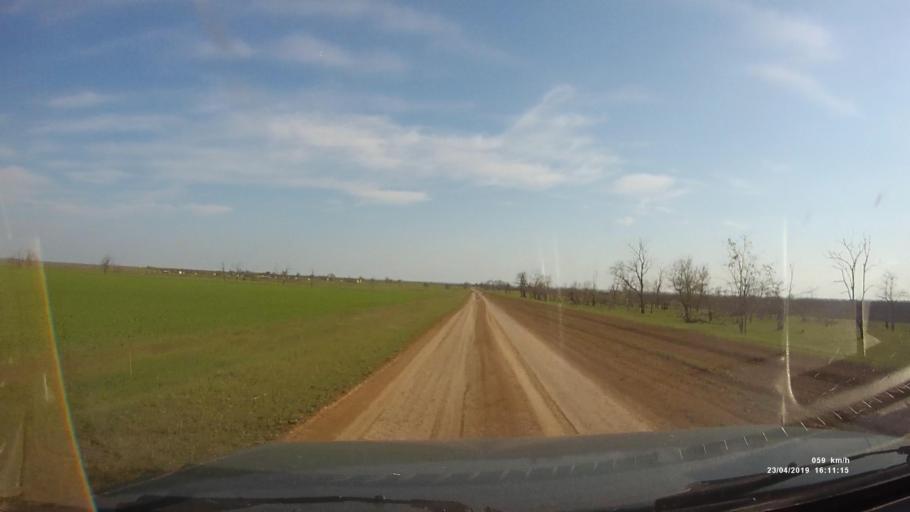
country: RU
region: Rostov
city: Remontnoye
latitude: 46.4754
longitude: 43.1231
